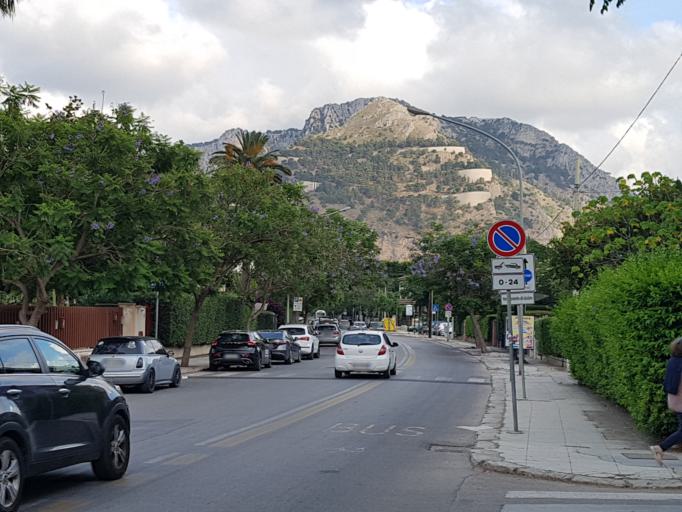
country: IT
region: Sicily
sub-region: Palermo
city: Palermo
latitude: 38.2008
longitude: 13.3262
